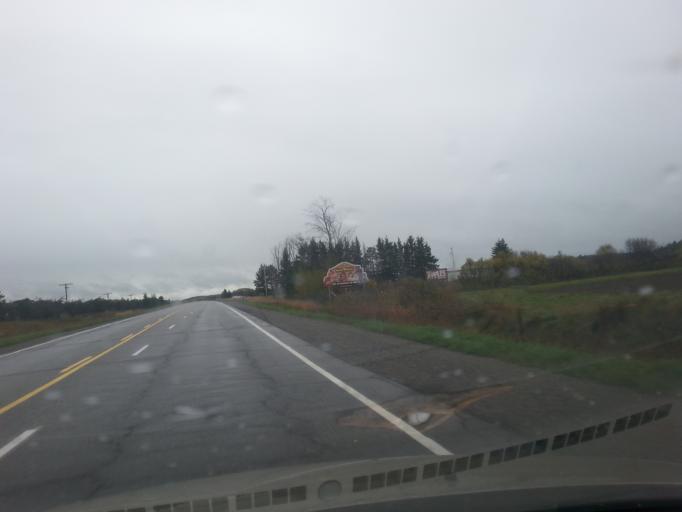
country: CA
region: Ontario
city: Greater Sudbury
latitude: 46.4331
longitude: -80.2616
